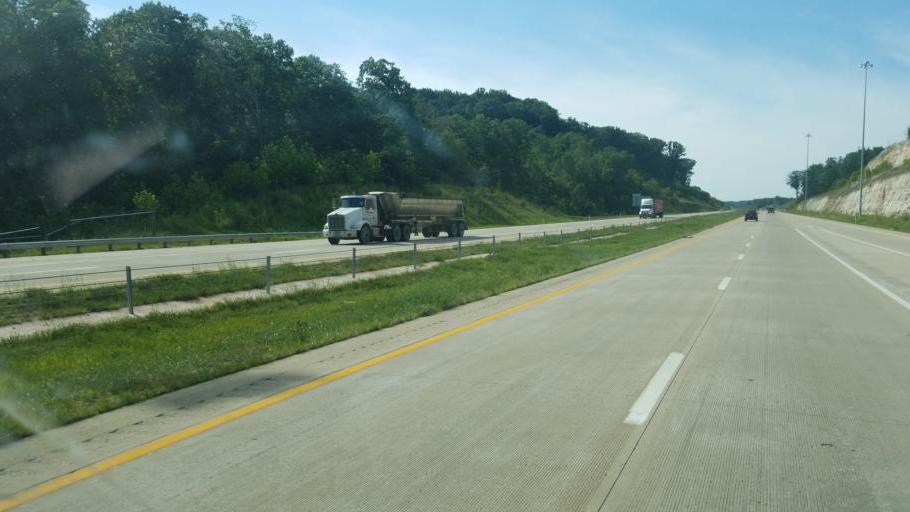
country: US
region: Ohio
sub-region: Athens County
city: Nelsonville
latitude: 39.4462
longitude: -82.2075
